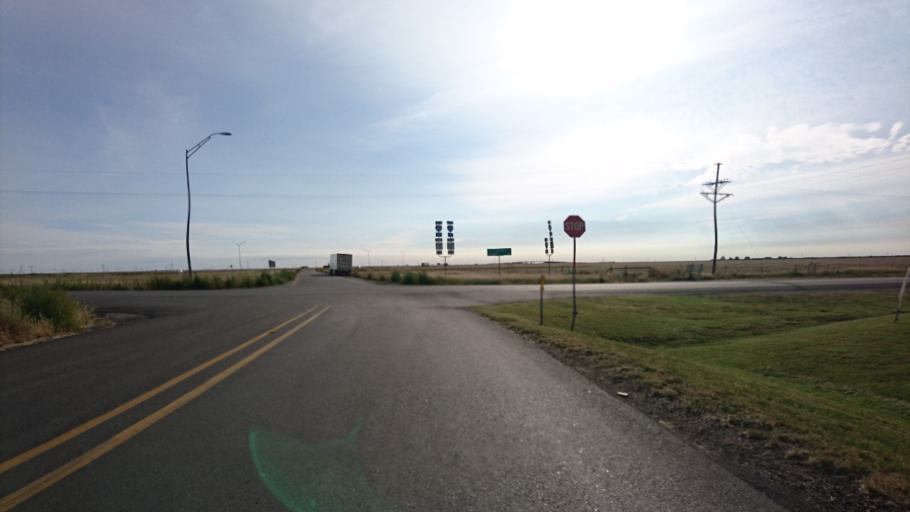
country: US
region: Texas
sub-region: Armstrong County
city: Claude
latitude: 35.2152
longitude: -101.3829
